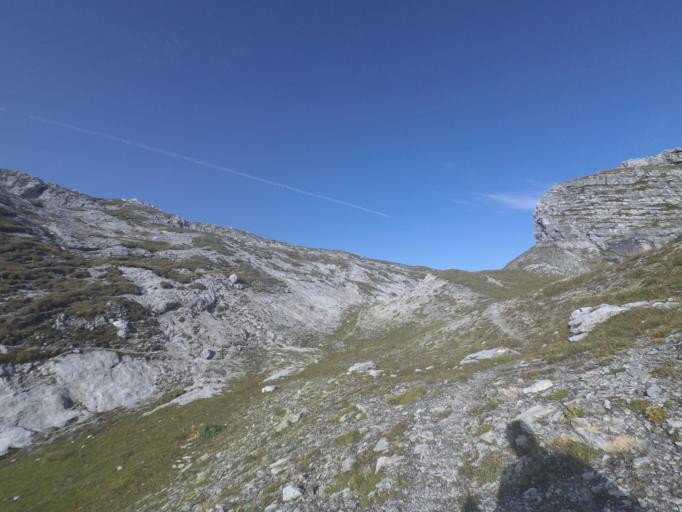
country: AT
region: Salzburg
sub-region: Politischer Bezirk Sankt Johann im Pongau
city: Kleinarl
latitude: 47.2220
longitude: 13.4136
